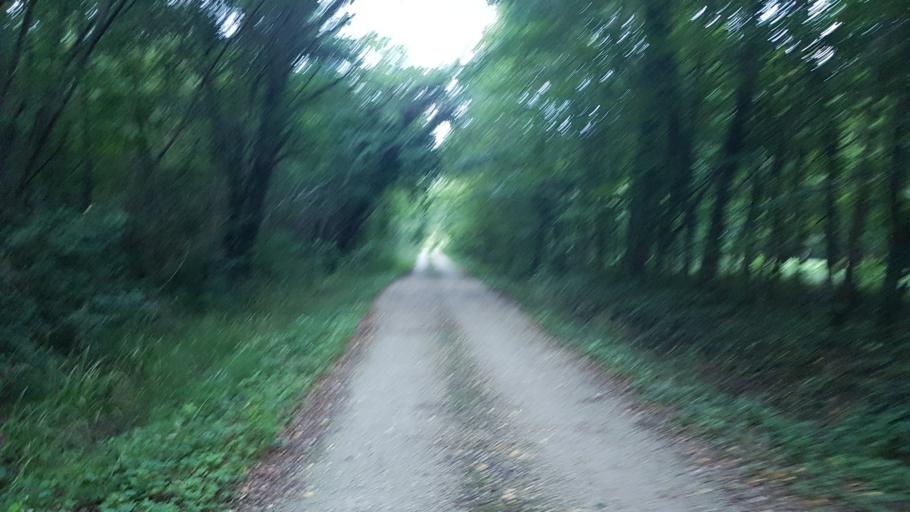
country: IT
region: Friuli Venezia Giulia
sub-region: Provincia di Gorizia
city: San Lorenzo Isontino
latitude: 45.9415
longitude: 13.5345
